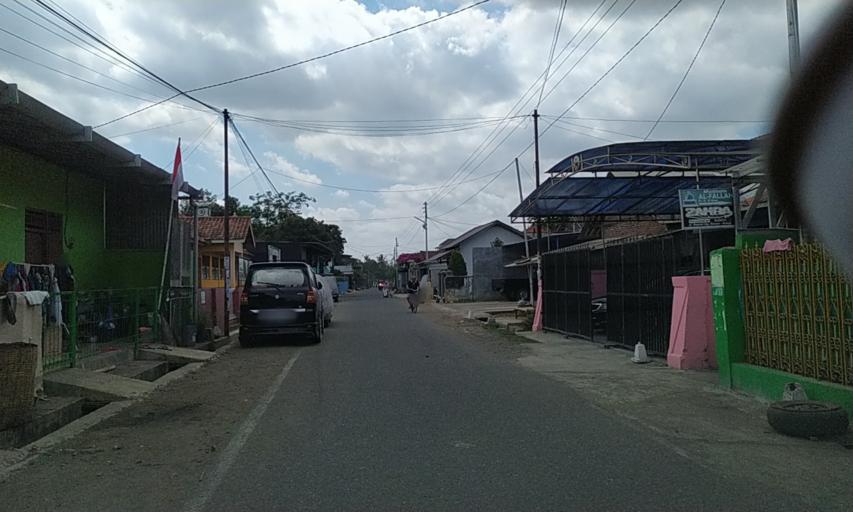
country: ID
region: Central Java
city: Kroya
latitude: -7.6334
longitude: 109.2493
